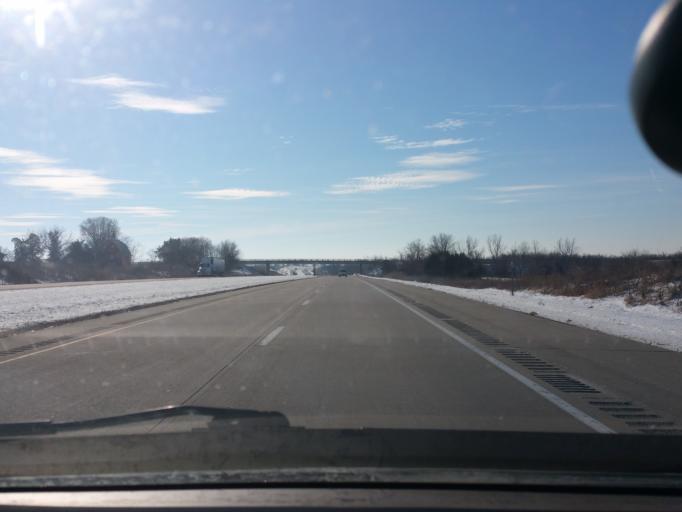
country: US
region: Iowa
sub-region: Clarke County
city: Osceola
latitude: 40.9166
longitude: -93.7974
